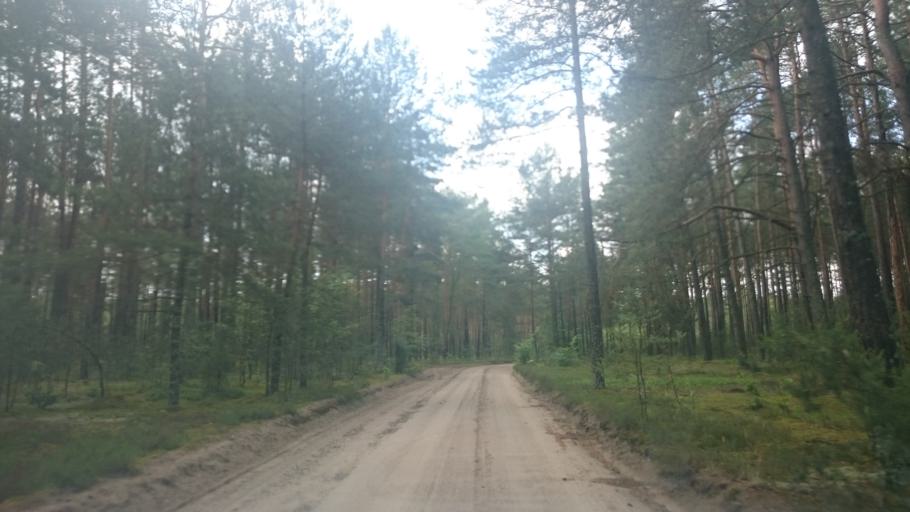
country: PL
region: Pomeranian Voivodeship
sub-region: Powiat koscierski
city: Karsin
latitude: 53.9874
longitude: 17.9321
